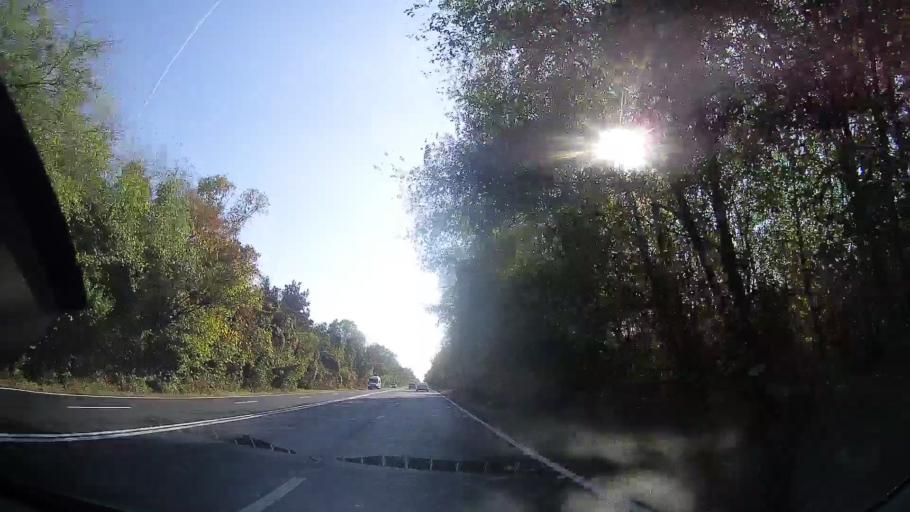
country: RO
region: Constanta
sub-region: Comuna Douazeci si Trei August
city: Dulcesti
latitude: 43.8700
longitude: 28.5746
